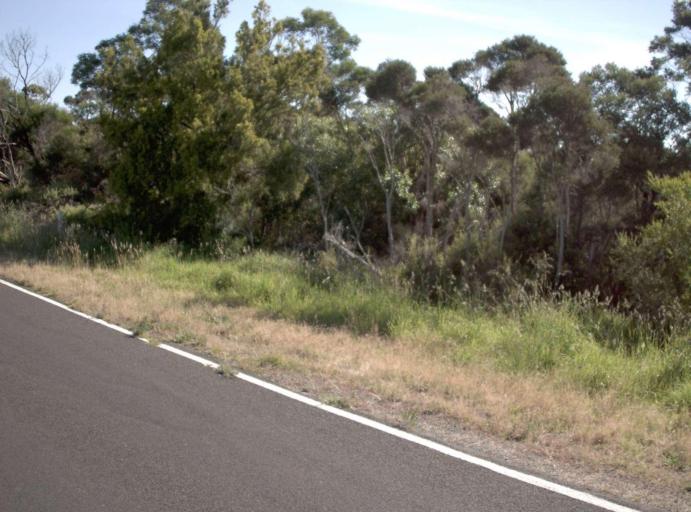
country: AU
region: Victoria
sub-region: Latrobe
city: Traralgon
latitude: -38.6425
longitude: 146.6711
